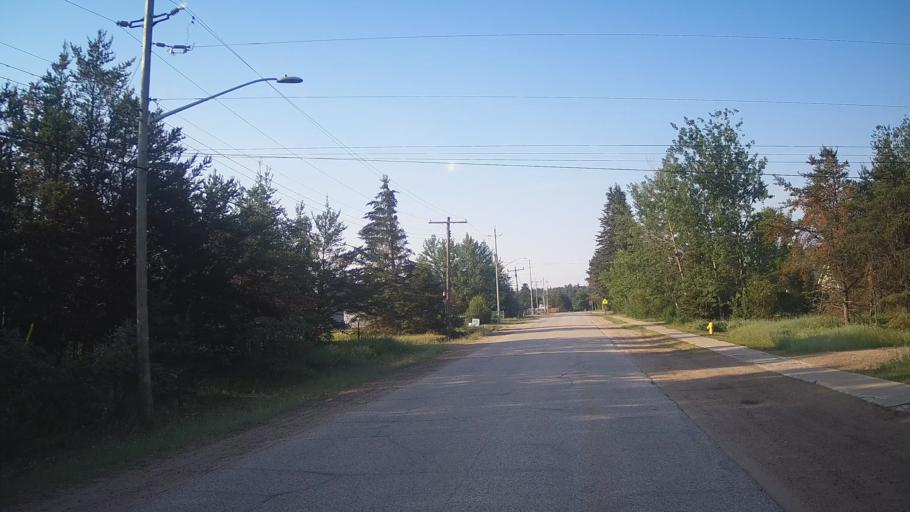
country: CA
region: Ontario
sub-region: Rainy River District
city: Atikokan
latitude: 49.4117
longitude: -91.6574
